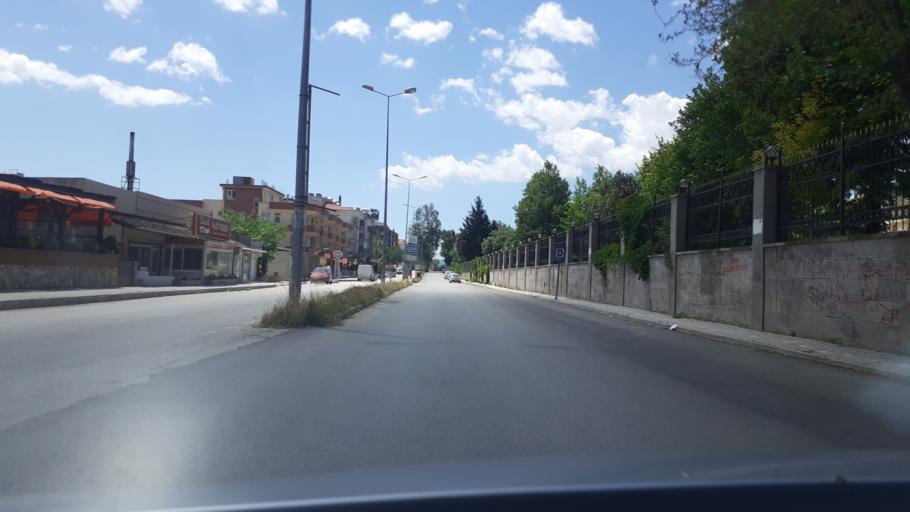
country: TR
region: Hatay
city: Anayazi
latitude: 36.3312
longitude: 36.1994
